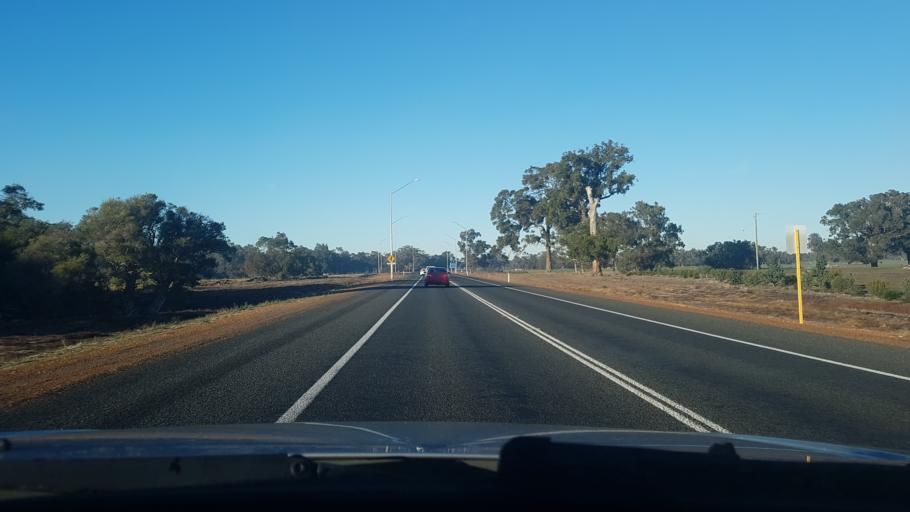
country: AU
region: Western Australia
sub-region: Busselton
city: Vasse
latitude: -33.6816
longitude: 115.2300
